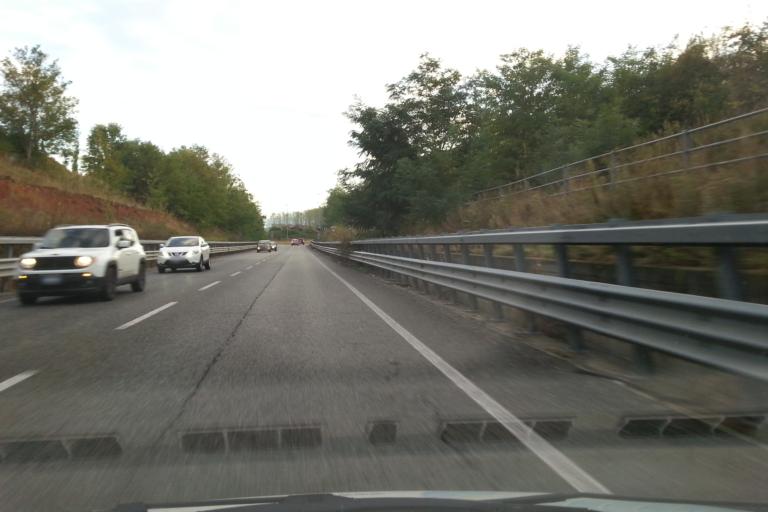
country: IT
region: Piedmont
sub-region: Provincia di Torino
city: Pasta
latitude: 45.0282
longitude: 7.5528
